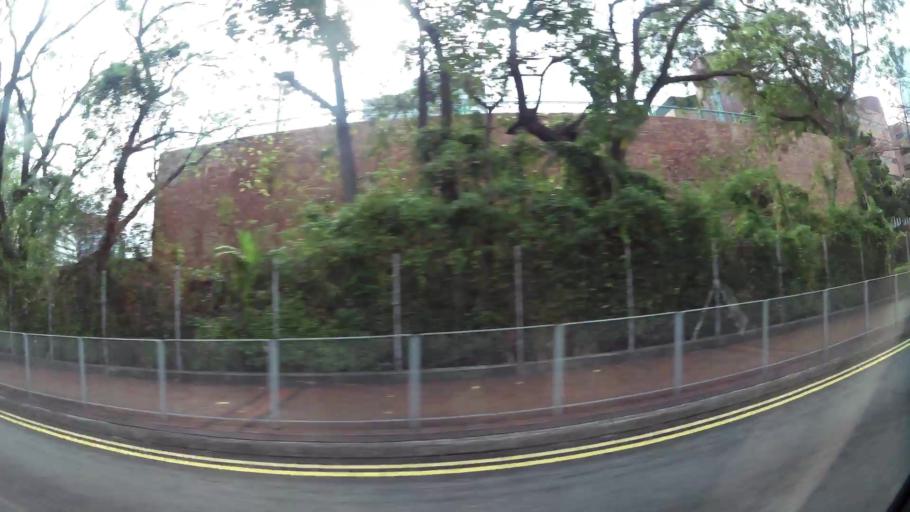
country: HK
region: Kowloon City
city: Kowloon
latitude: 22.3044
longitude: 114.1783
